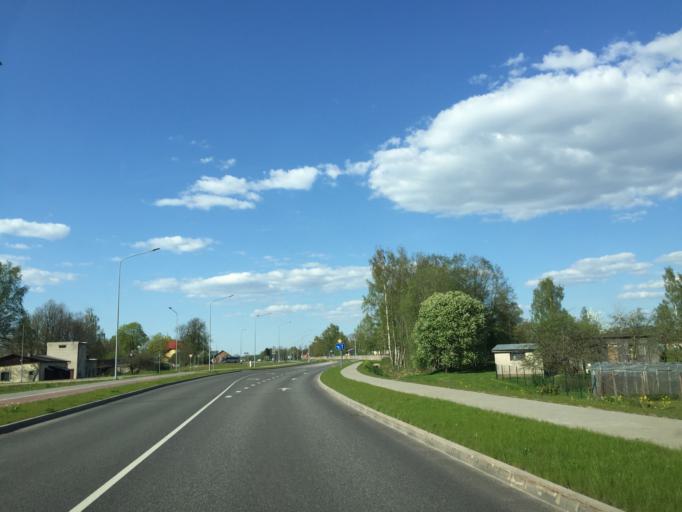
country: LV
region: Limbazu Rajons
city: Limbazi
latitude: 57.5063
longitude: 24.7214
